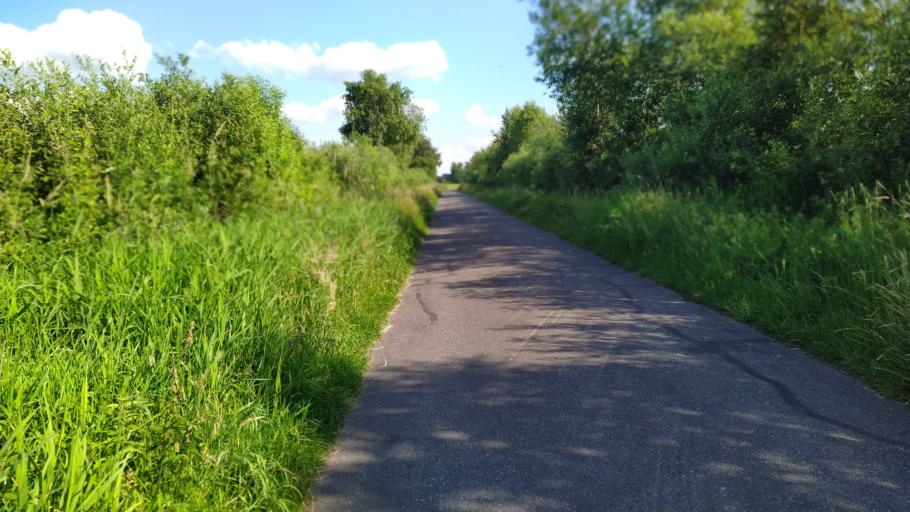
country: DE
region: Lower Saxony
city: Lintig
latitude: 53.6191
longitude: 8.8687
